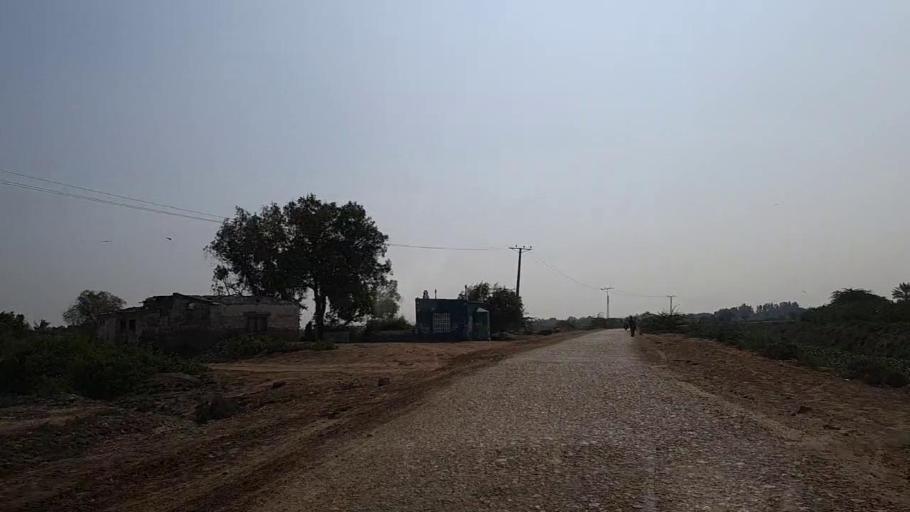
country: PK
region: Sindh
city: Thatta
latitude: 24.7380
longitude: 67.7702
